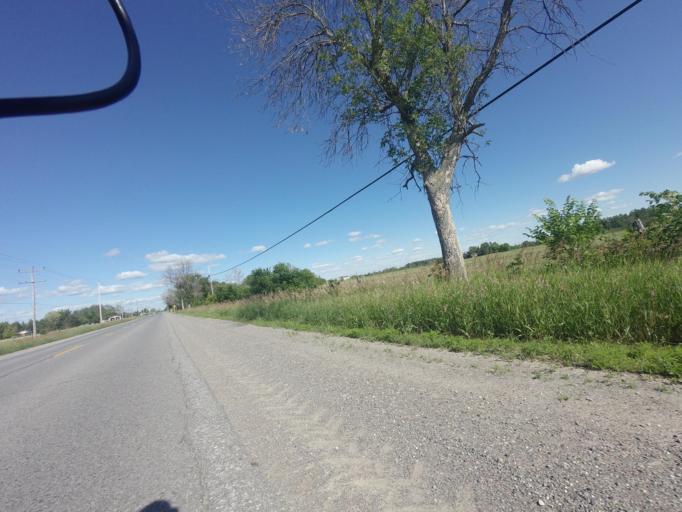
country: CA
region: Ontario
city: Arnprior
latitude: 45.4170
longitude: -76.4092
